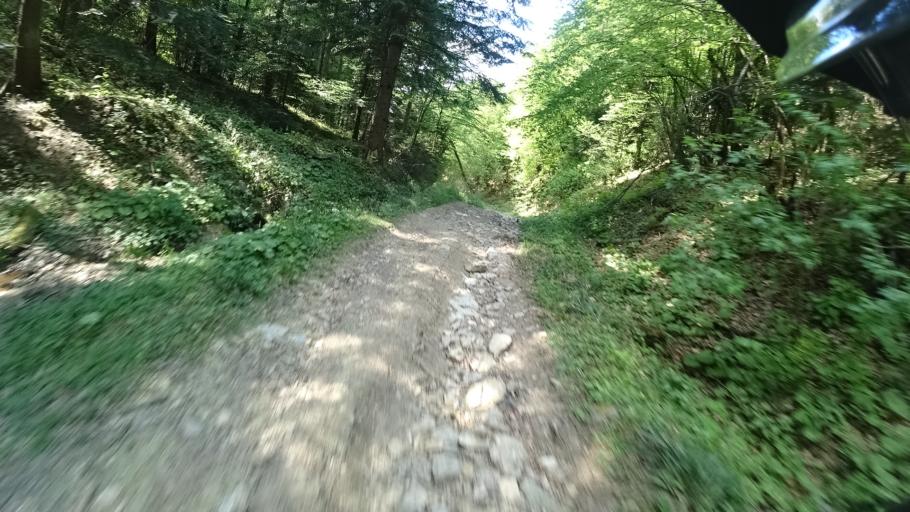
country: HR
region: Grad Zagreb
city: Kasina
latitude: 45.9451
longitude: 16.0175
